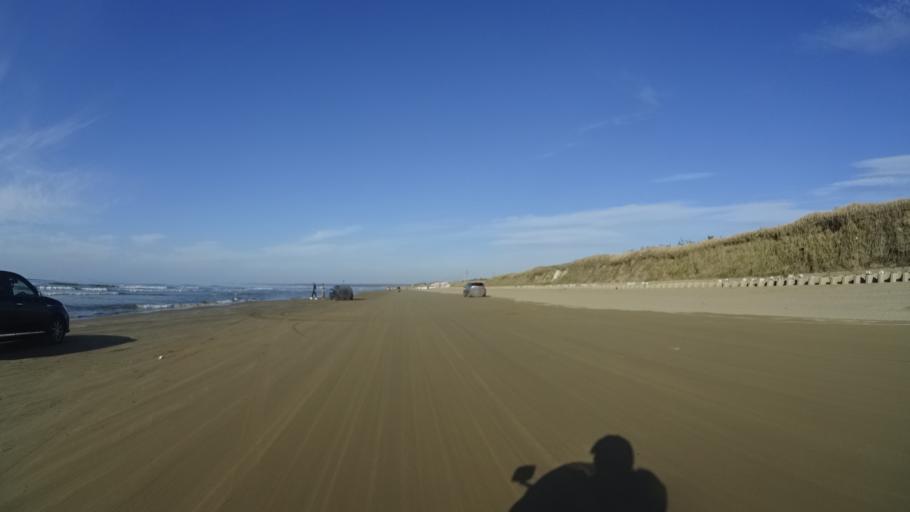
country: JP
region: Ishikawa
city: Hakui
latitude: 36.8486
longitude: 136.7527
